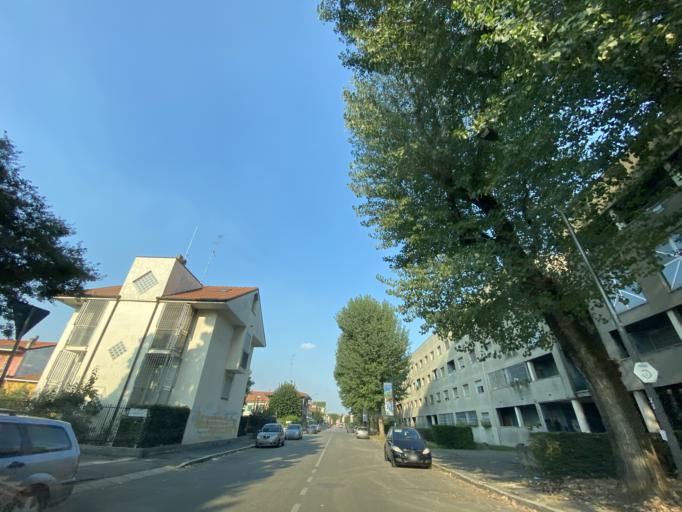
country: IT
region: Lombardy
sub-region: Citta metropolitana di Milano
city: Novate Milanese
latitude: 45.5151
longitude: 9.1501
